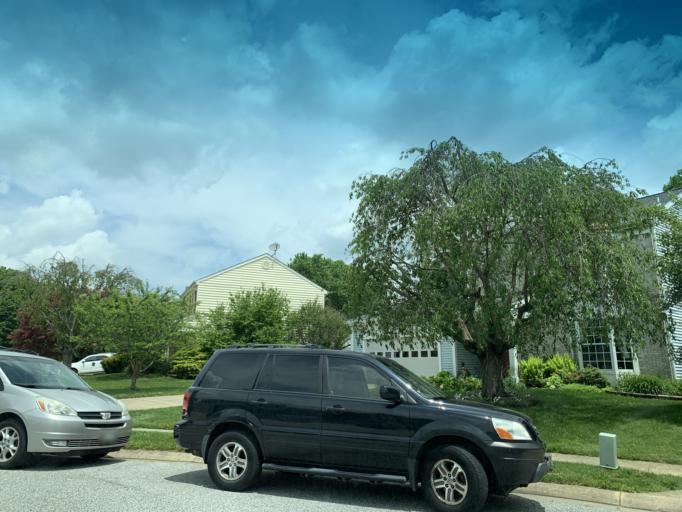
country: US
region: Maryland
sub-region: Harford County
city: South Bel Air
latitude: 39.5499
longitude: -76.3263
